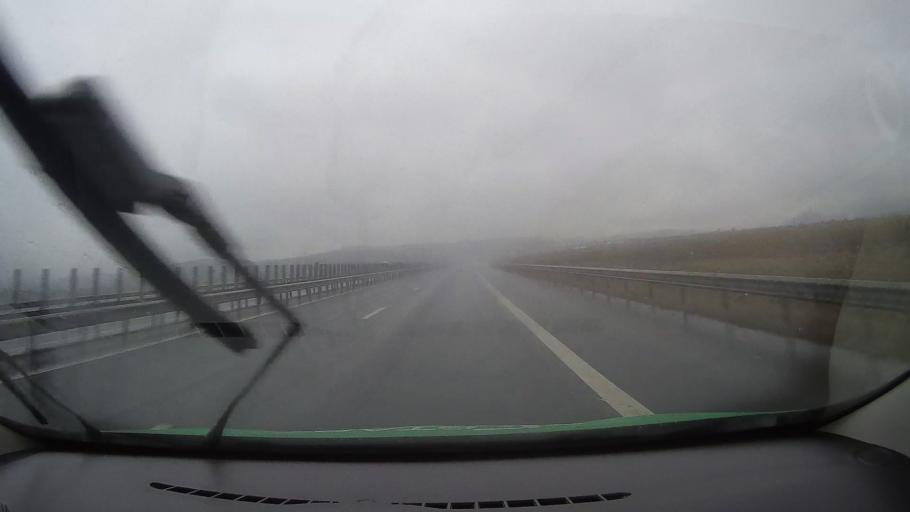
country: RO
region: Sibiu
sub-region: Oras Saliste
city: Saliste
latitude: 45.7956
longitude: 23.9346
